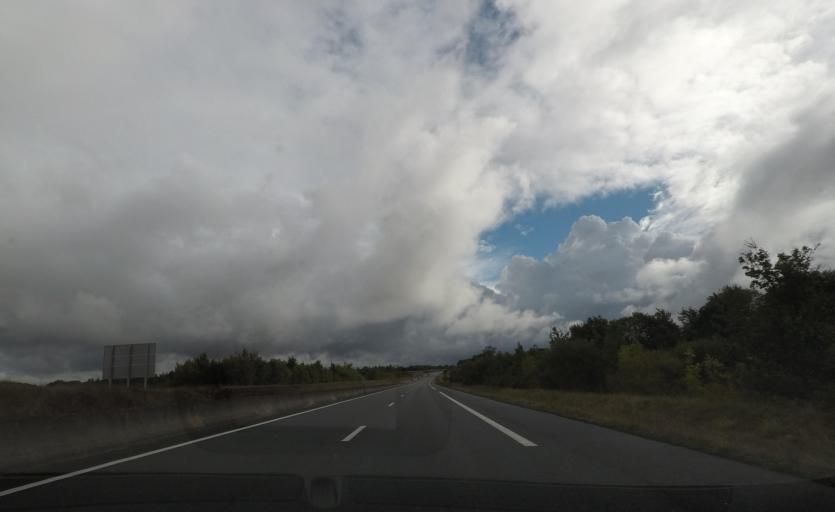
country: FR
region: Pays de la Loire
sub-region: Departement de la Vendee
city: La Roche-sur-Yon
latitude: 46.6493
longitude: -1.3886
